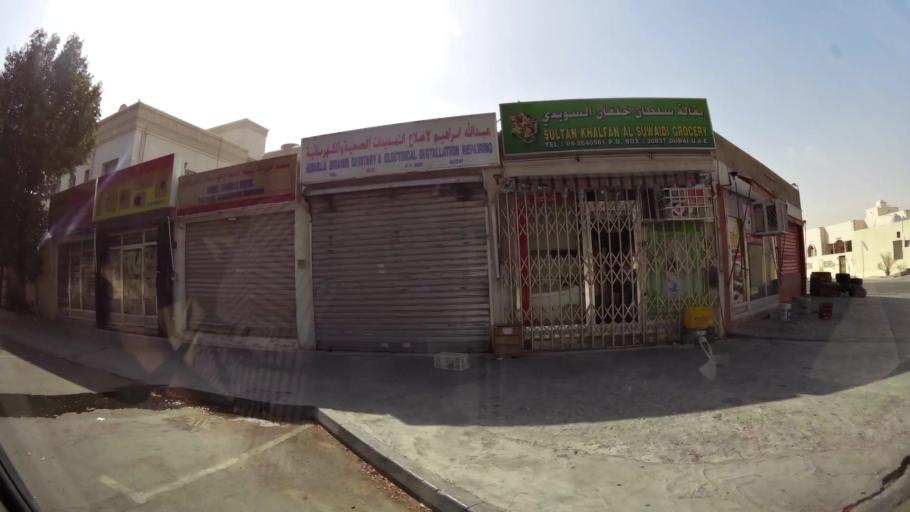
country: AE
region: Ash Shariqah
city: Sharjah
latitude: 25.2634
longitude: 55.3925
